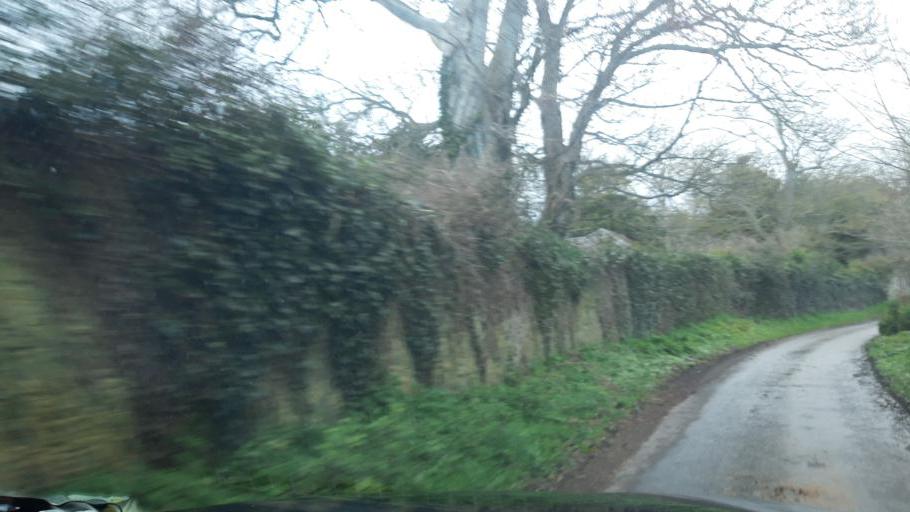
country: IE
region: Leinster
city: Donabate
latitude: 53.4708
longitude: -6.1721
